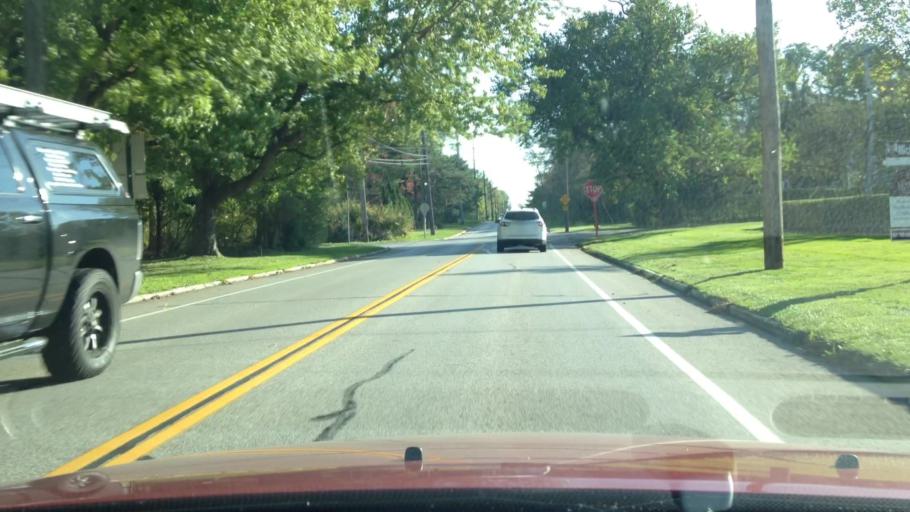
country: US
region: Ohio
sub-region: Cuyahoga County
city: Pepper Pike
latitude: 41.4791
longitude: -81.4634
